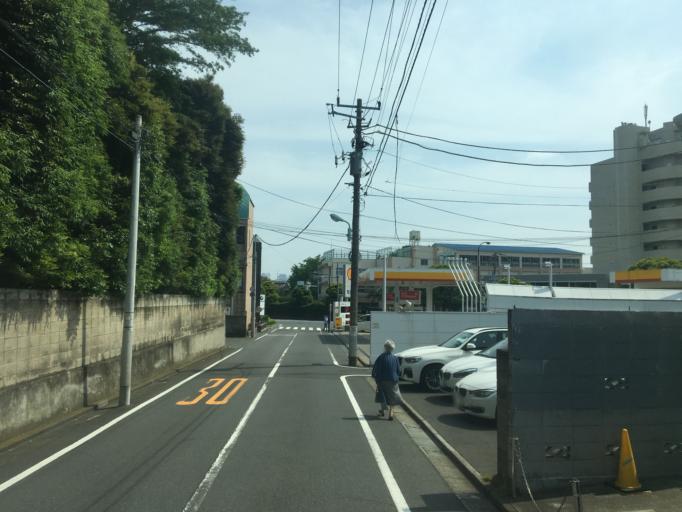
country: JP
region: Tokyo
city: Tokyo
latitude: 35.7355
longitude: 139.6942
